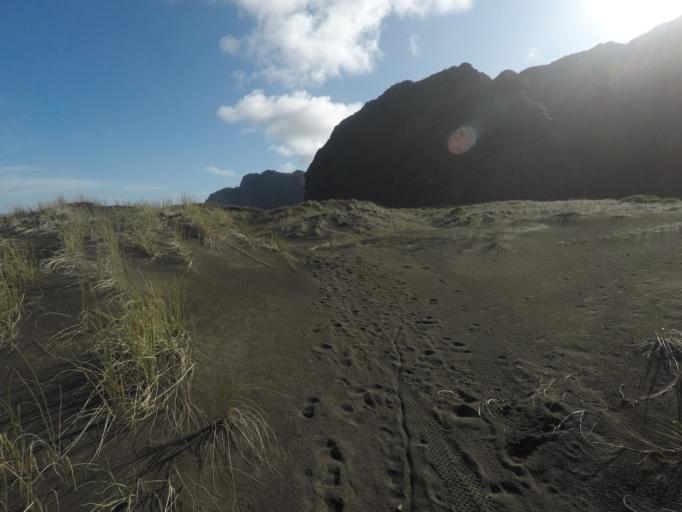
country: NZ
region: Auckland
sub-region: Auckland
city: Muriwai Beach
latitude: -36.9954
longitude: 174.4740
